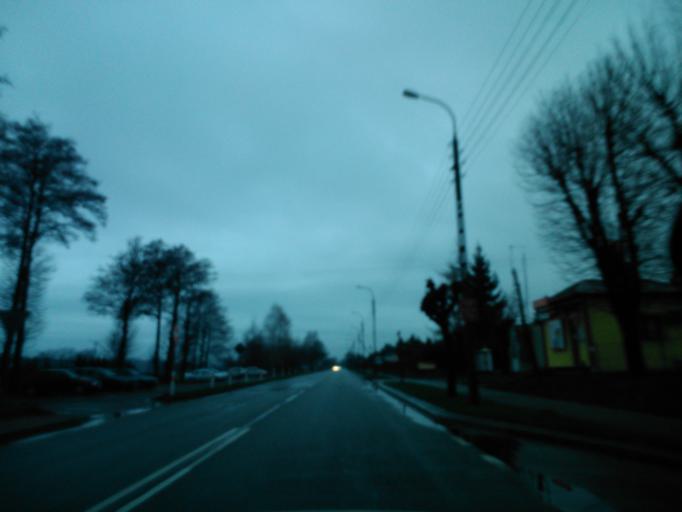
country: PL
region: Lublin Voivodeship
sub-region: Powiat krasnicki
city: Krasnik
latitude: 50.9128
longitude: 22.2502
